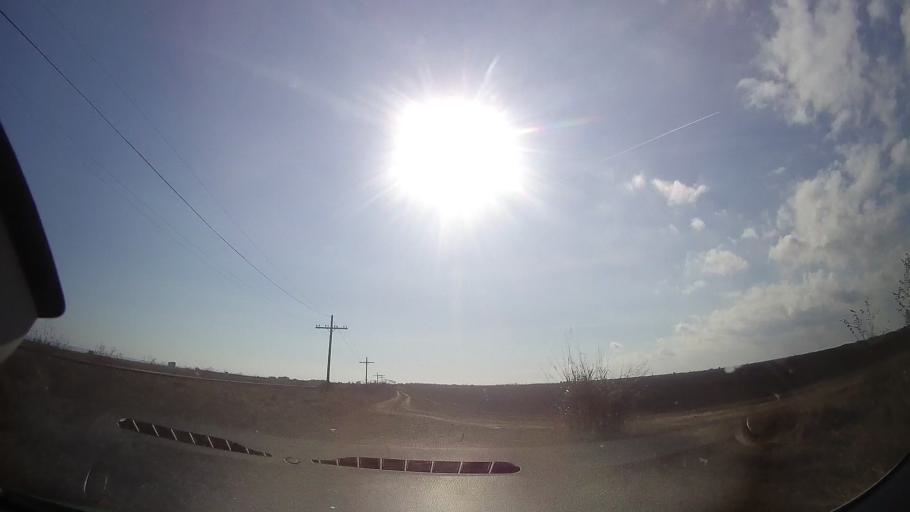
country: RO
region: Constanta
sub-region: Comuna Tuzla
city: Tuzla
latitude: 43.9831
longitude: 28.6446
